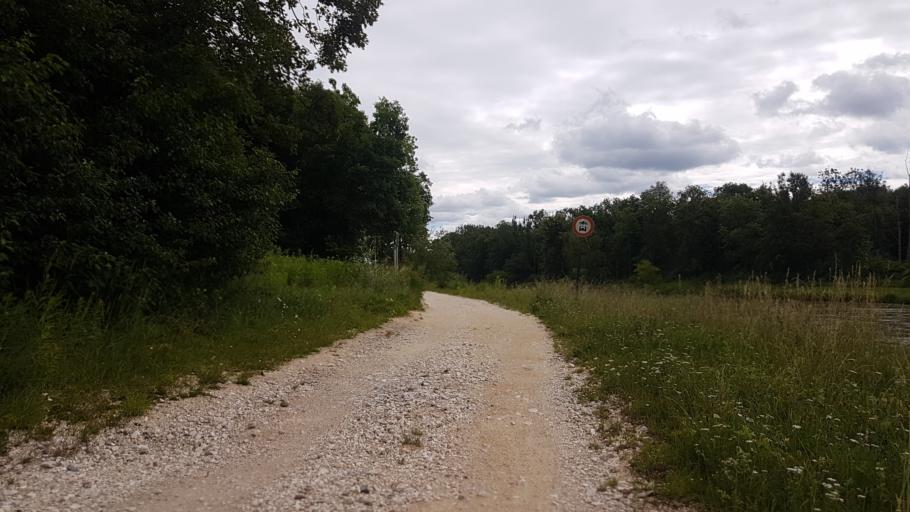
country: DE
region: Bavaria
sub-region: Swabia
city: Offingen
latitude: 48.4873
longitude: 10.3429
